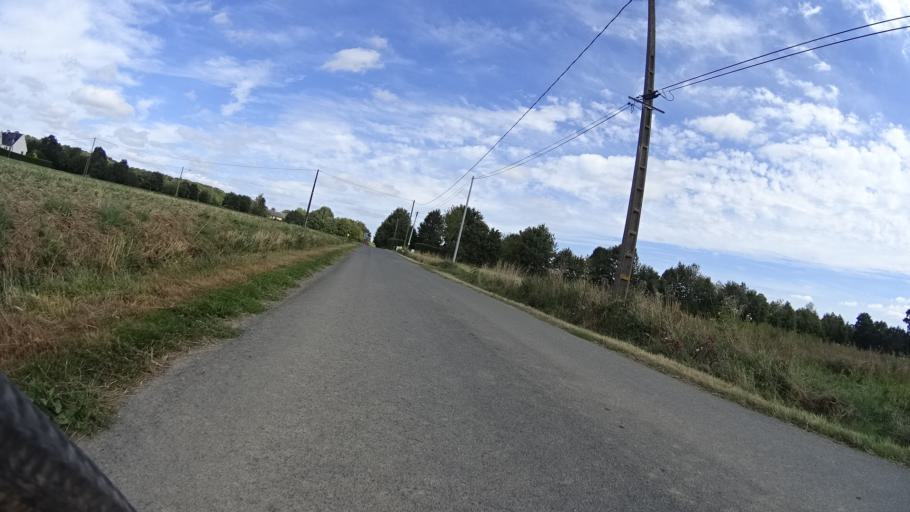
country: FR
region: Brittany
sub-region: Departement d'Ille-et-Vilaine
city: La Meziere
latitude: 48.2364
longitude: -1.7522
